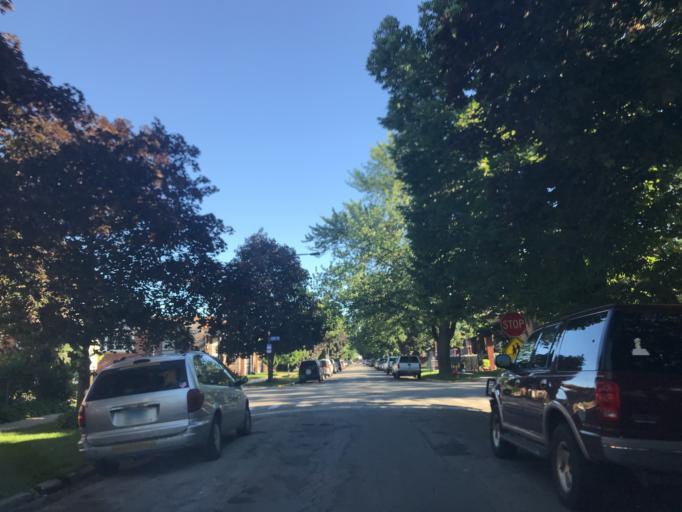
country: US
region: Illinois
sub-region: Cook County
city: Cicero
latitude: 41.8478
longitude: -87.7663
